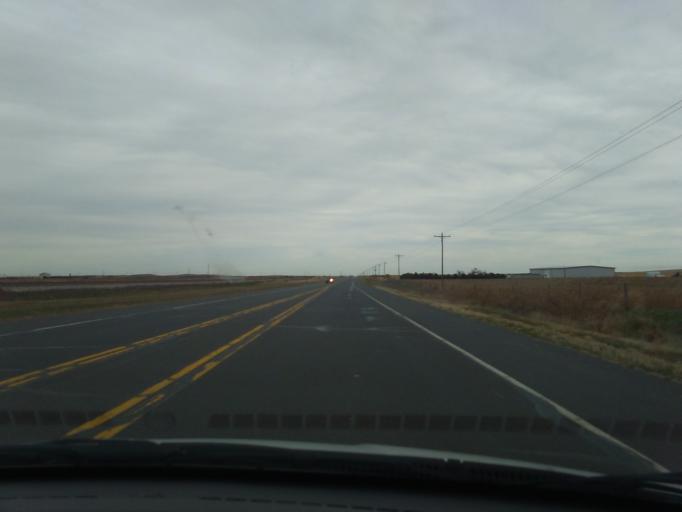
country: US
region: Colorado
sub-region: Yuma County
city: Yuma
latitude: 40.1132
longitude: -102.5970
